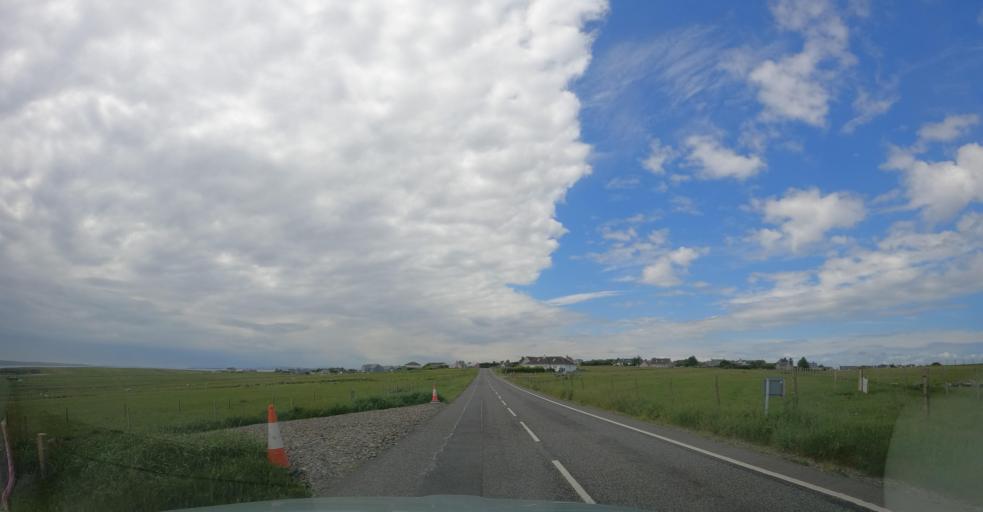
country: GB
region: Scotland
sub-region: Eilean Siar
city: Isle of Lewis
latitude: 58.2800
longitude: -6.2853
